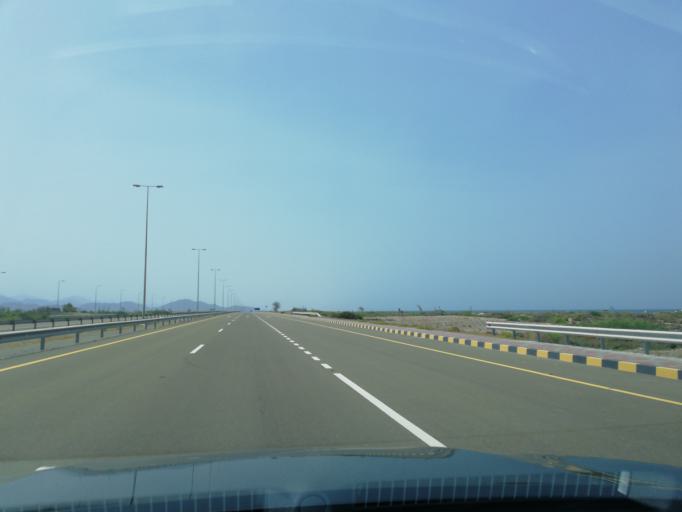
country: OM
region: Al Batinah
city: Shinas
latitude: 24.9027
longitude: 56.3956
